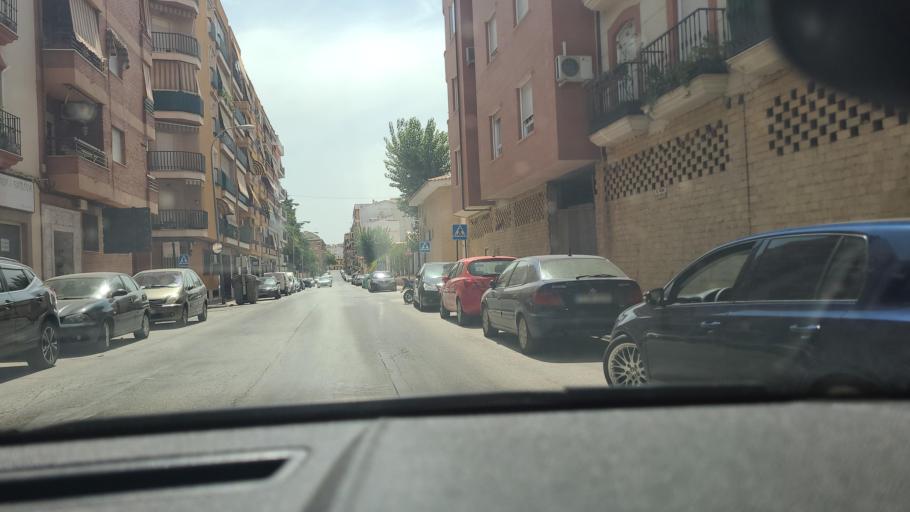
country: ES
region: Andalusia
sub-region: Provincia de Jaen
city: Linares
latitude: 38.0940
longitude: -3.6281
